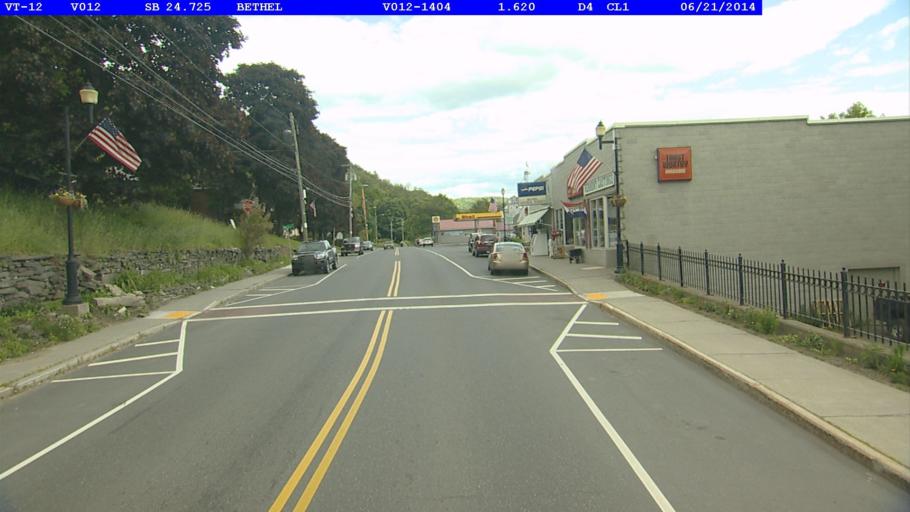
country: US
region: Vermont
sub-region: Orange County
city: Randolph
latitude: 43.8309
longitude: -72.6333
